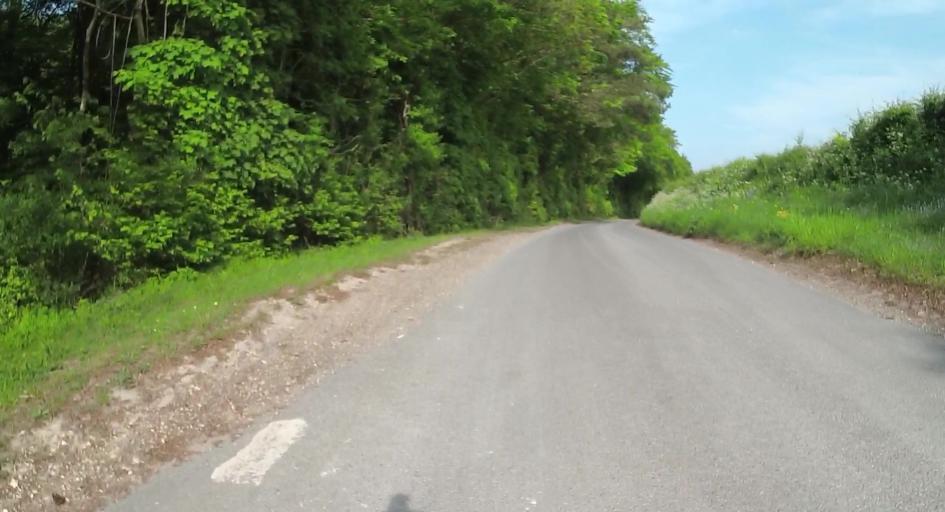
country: GB
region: England
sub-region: Hampshire
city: Kingsclere
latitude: 51.3309
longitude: -1.2995
